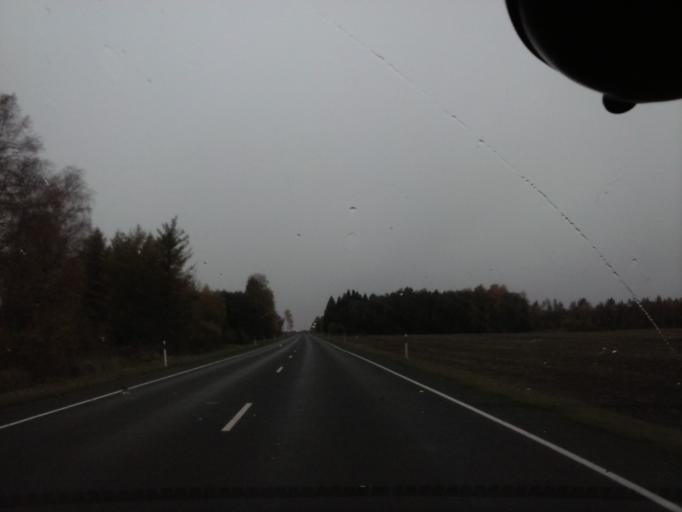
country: EE
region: Viljandimaa
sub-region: Vohma linn
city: Vohma
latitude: 58.7129
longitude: 25.6146
